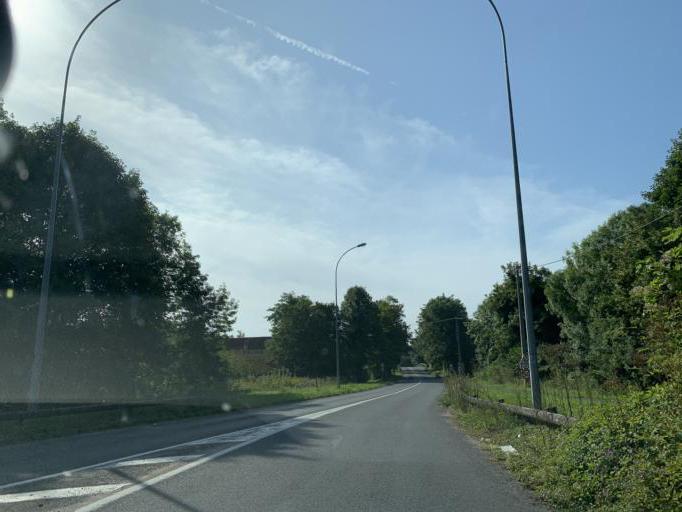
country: FR
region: Ile-de-France
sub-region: Departement de Seine-et-Marne
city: Annet-sur-Marne
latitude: 48.9231
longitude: 2.7238
